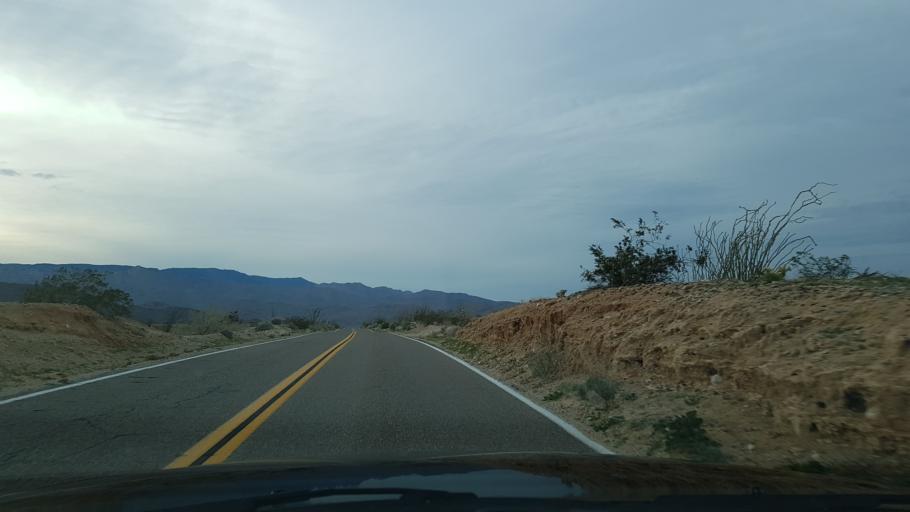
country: MX
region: Baja California
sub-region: Tecate
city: Cereso del Hongo
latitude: 32.8204
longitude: -116.1516
